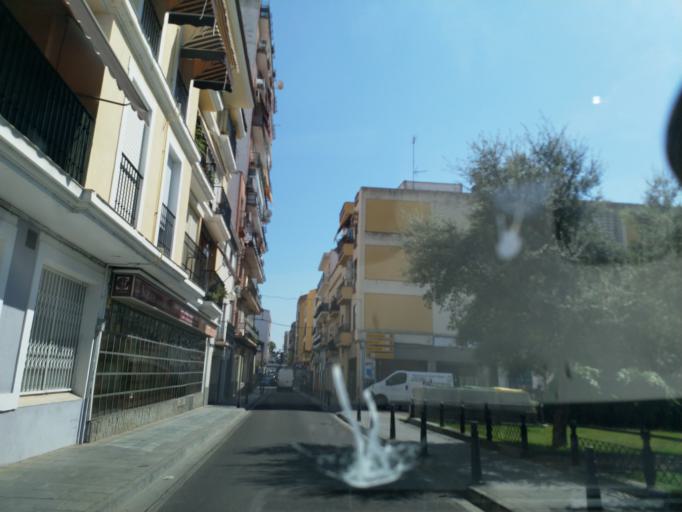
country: ES
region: Extremadura
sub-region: Provincia de Badajoz
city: Merida
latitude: 38.9143
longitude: -6.3454
